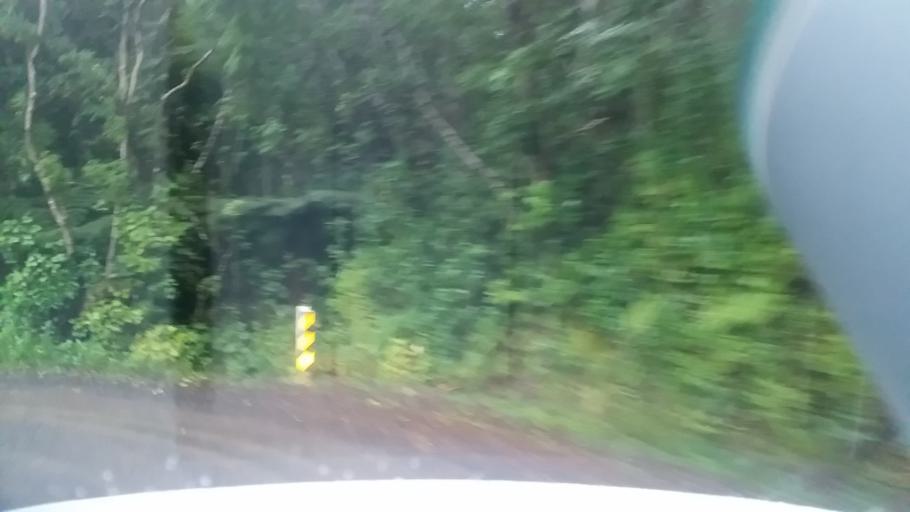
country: NZ
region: Canterbury
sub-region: Christchurch City
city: Christchurch
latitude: -43.8062
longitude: 172.8905
